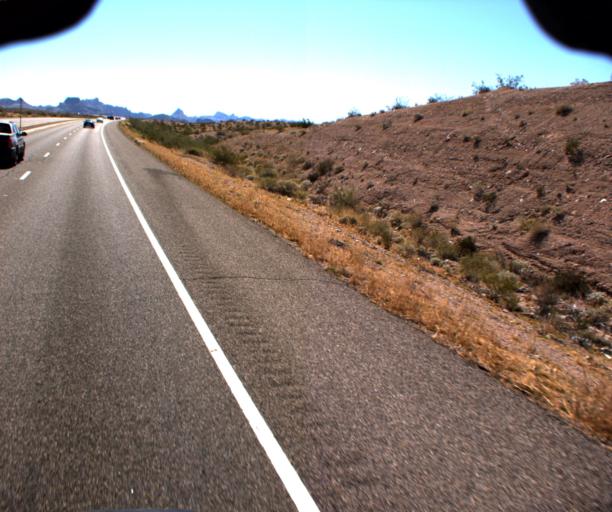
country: US
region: Nevada
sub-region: Clark County
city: Laughlin
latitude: 35.1886
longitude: -114.5095
